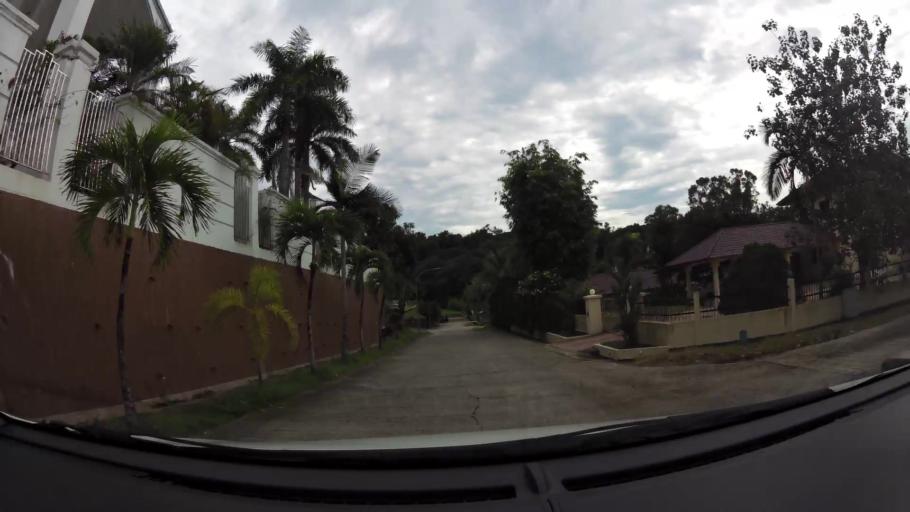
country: BN
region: Brunei and Muara
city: Bandar Seri Begawan
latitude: 4.8714
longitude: 114.8993
